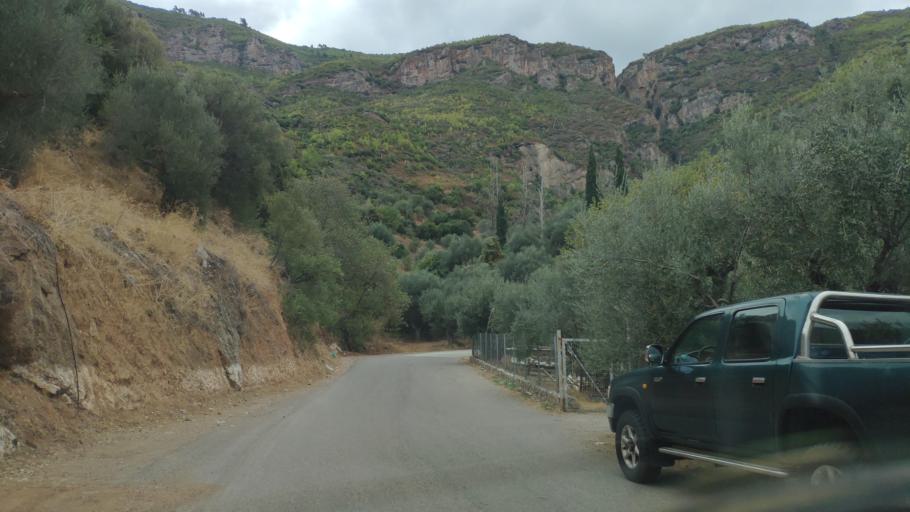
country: GR
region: West Greece
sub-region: Nomos Achaias
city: Temeni
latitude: 38.1761
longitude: 22.1443
